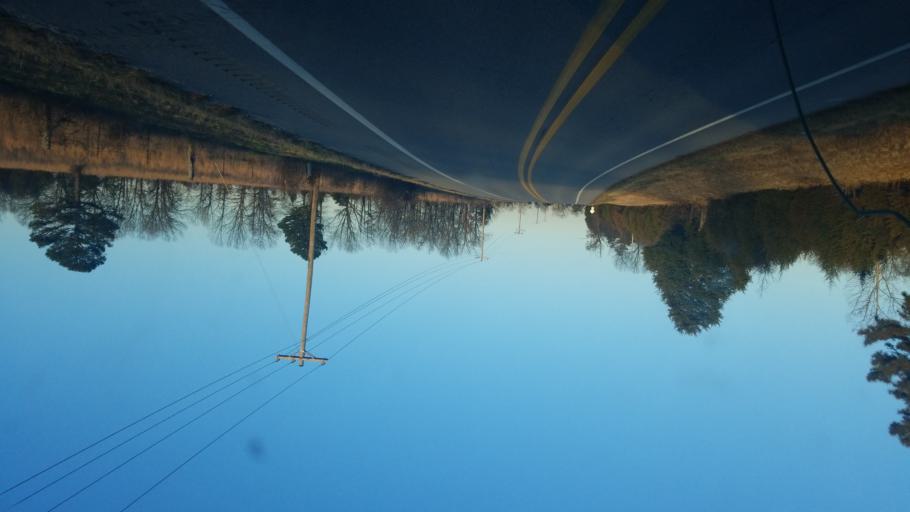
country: US
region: Arkansas
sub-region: Baxter County
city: Mountain Home
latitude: 36.3757
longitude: -92.1381
